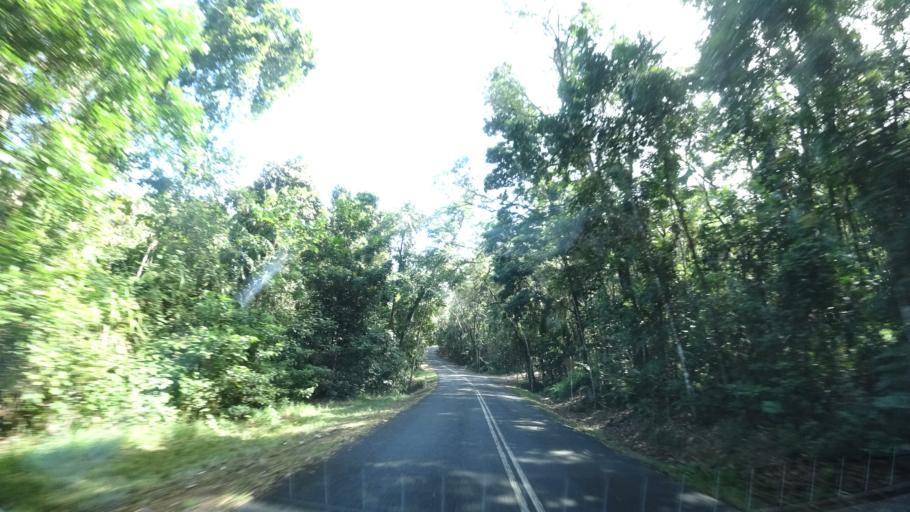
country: AU
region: Queensland
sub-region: Cairns
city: Port Douglas
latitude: -16.2625
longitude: 145.4288
